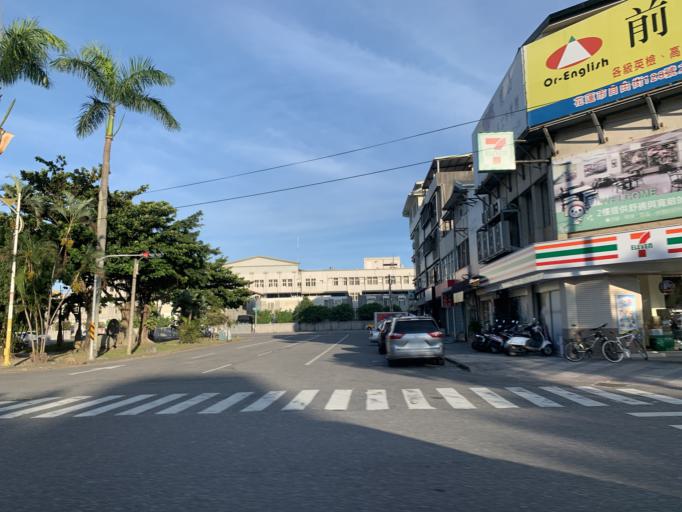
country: TW
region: Taiwan
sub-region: Hualien
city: Hualian
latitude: 23.9918
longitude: 121.6260
